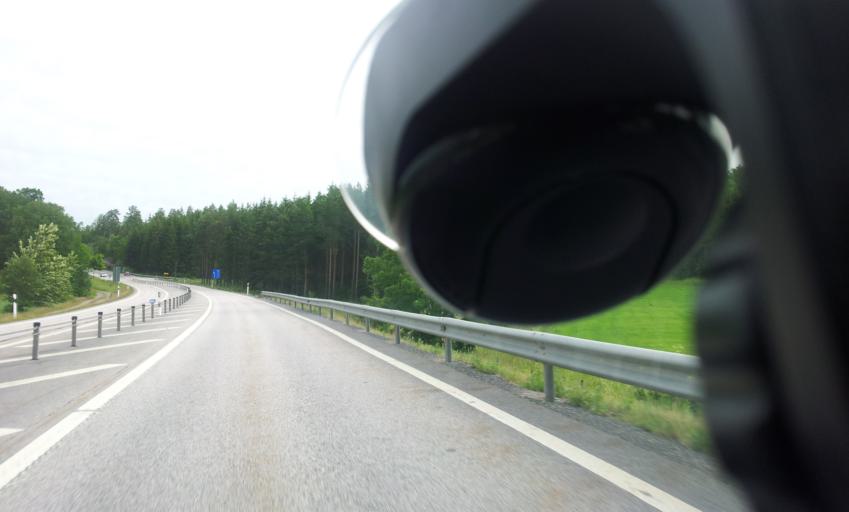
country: SE
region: Kalmar
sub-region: Vasterviks Kommun
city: Forserum
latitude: 58.0199
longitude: 16.5186
